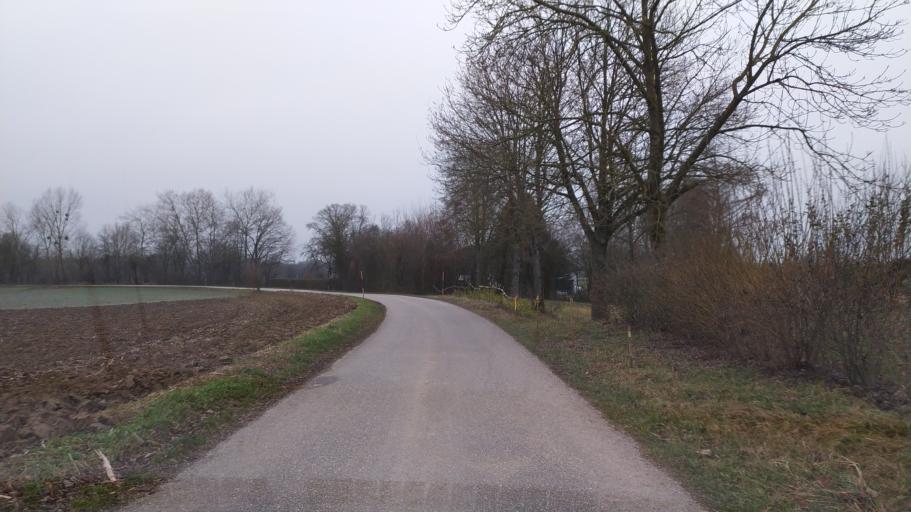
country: AT
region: Upper Austria
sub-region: Politischer Bezirk Perg
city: Perg
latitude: 48.2201
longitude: 14.7207
